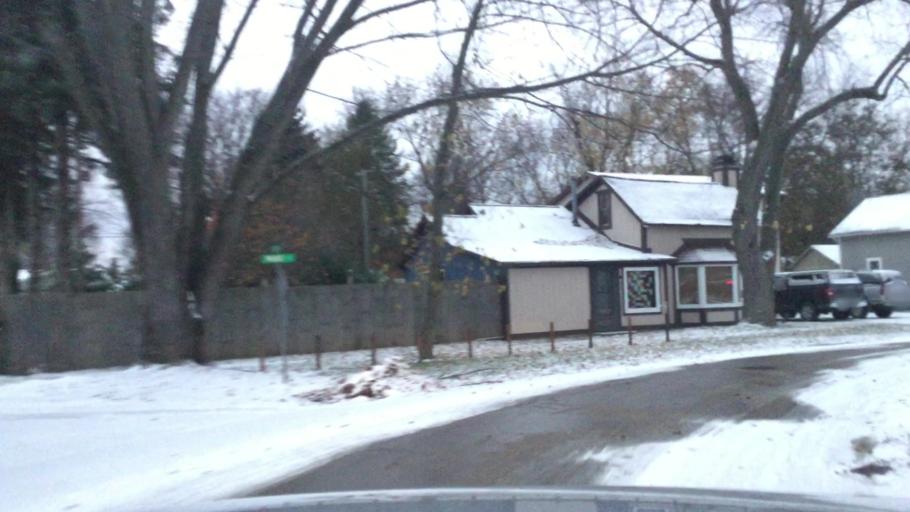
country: US
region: Michigan
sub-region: Livingston County
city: Brighton
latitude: 42.5326
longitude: -83.7888
